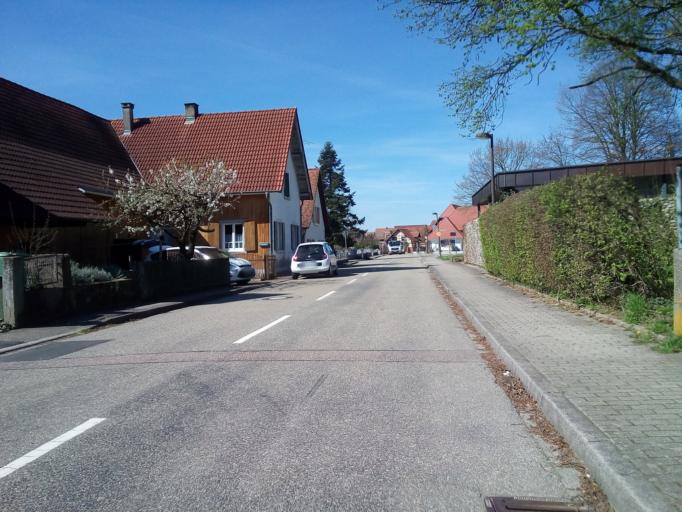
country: DE
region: Baden-Wuerttemberg
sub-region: Freiburg Region
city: Rheinau
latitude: 48.6526
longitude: 7.9286
